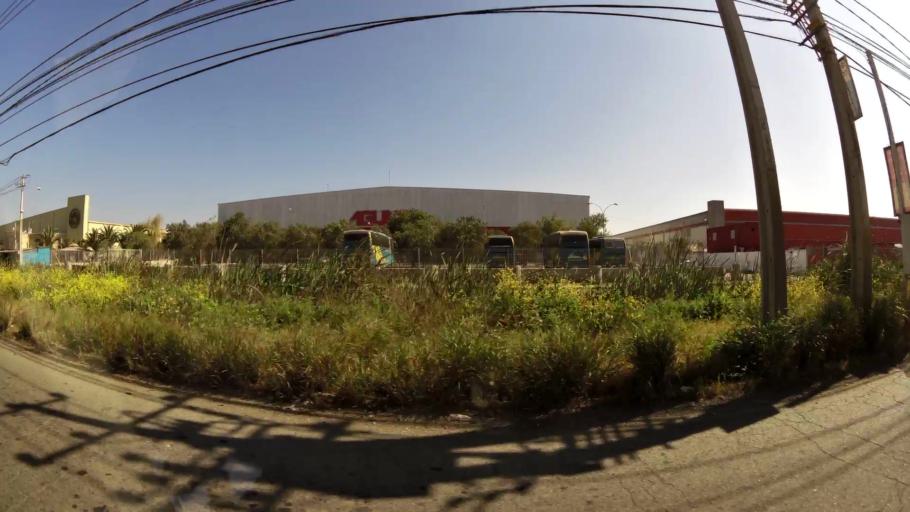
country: CL
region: Santiago Metropolitan
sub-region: Provincia de Chacabuco
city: Chicureo Abajo
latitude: -33.3213
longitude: -70.7374
